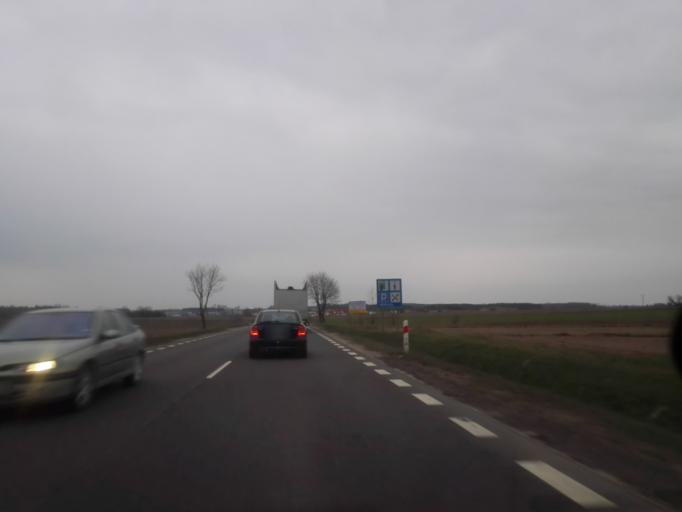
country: PL
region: Podlasie
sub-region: Powiat grajewski
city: Grajewo
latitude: 53.6318
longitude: 22.4209
